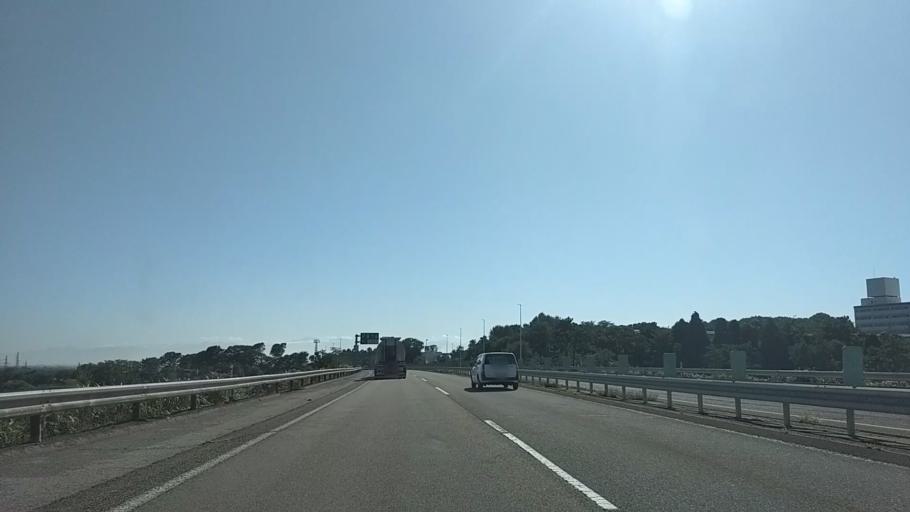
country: JP
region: Toyama
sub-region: Oyabe Shi
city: Oyabe
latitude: 36.6270
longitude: 136.8678
